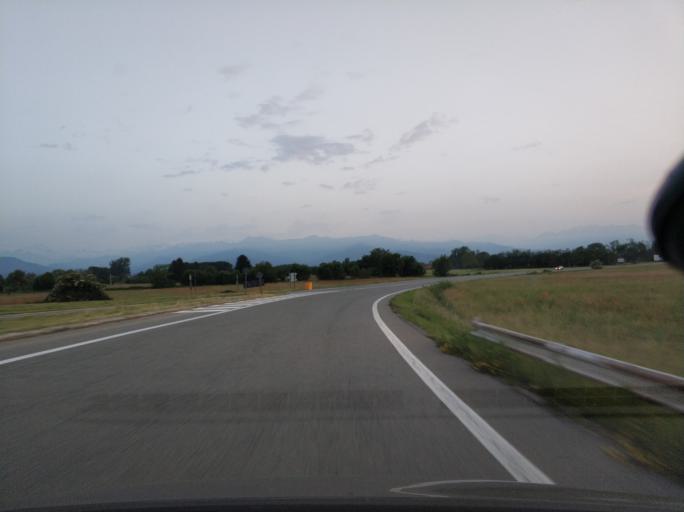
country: IT
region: Piedmont
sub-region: Provincia di Torino
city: Caselle Torinese
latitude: 45.1890
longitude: 7.6400
